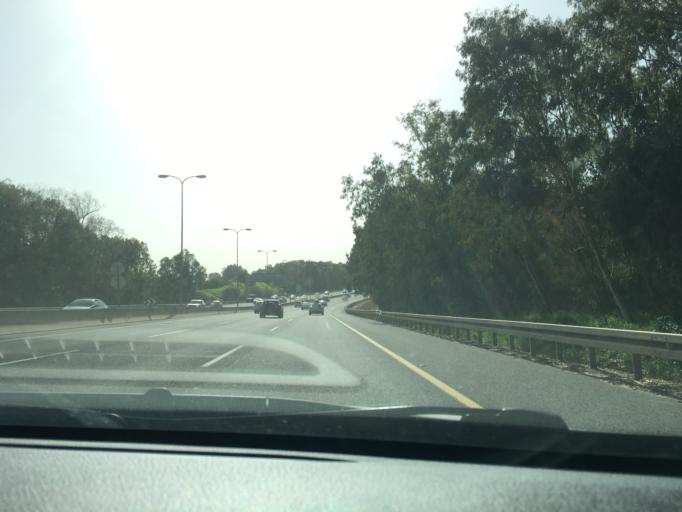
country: IL
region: Central District
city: Hod HaSharon
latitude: 32.1605
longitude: 34.8767
